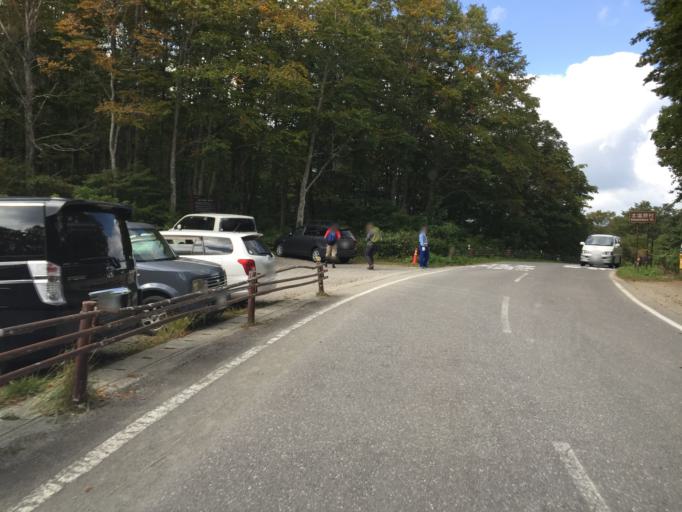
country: JP
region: Fukushima
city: Inawashiro
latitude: 37.6144
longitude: 140.0484
